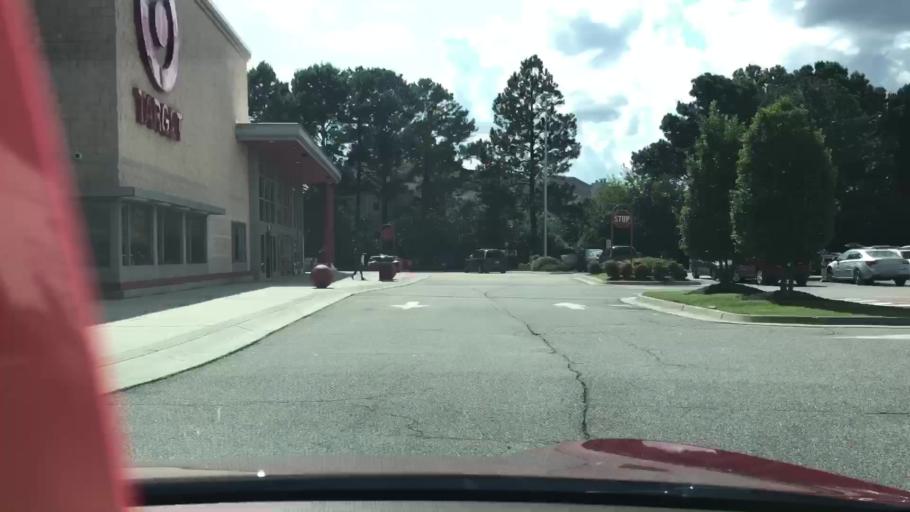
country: US
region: Virginia
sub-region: City of Virginia Beach
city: Virginia Beach
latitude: 36.8467
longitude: -76.0226
